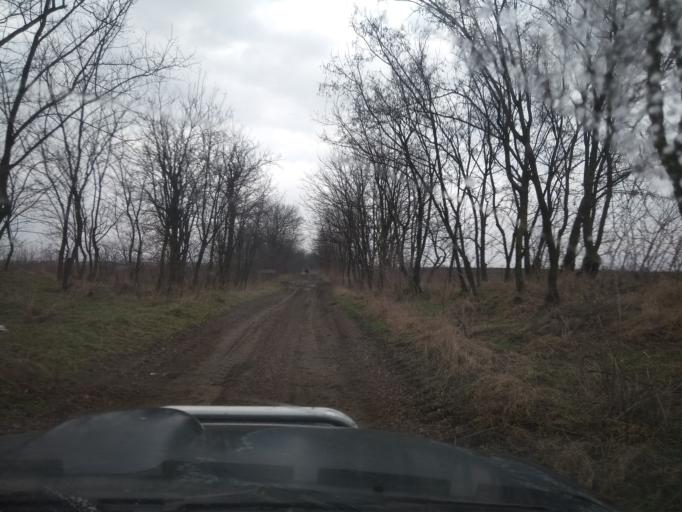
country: HU
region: Szabolcs-Szatmar-Bereg
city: Nagycserkesz
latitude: 47.9799
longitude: 21.5552
